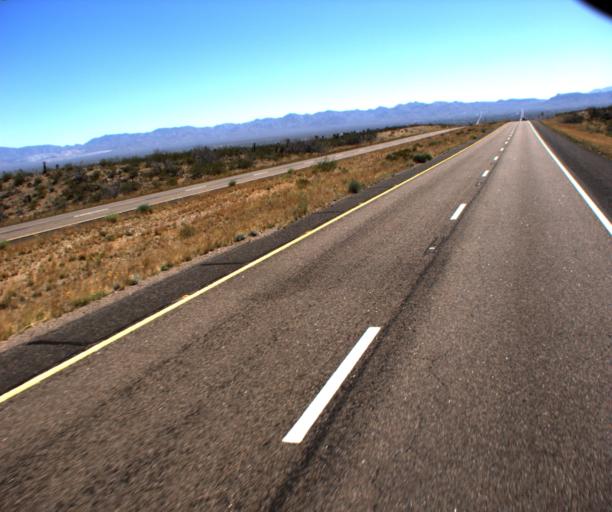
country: US
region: Arizona
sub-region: Mohave County
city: Golden Valley
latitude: 35.2282
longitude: -114.3465
